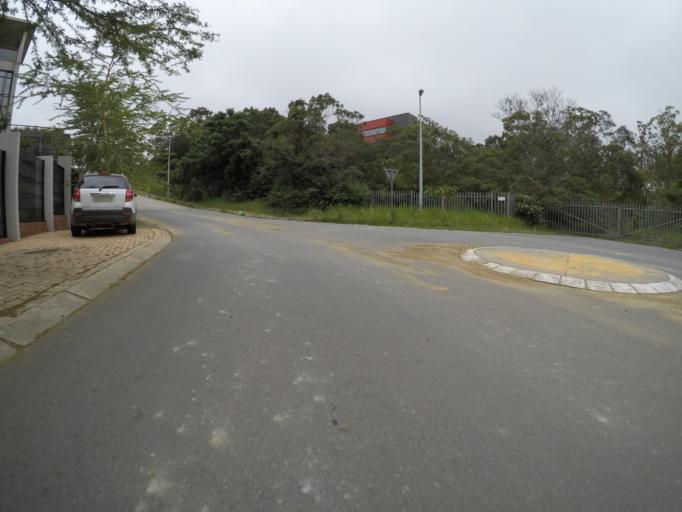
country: ZA
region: Eastern Cape
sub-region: Buffalo City Metropolitan Municipality
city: East London
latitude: -32.9477
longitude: 27.9407
